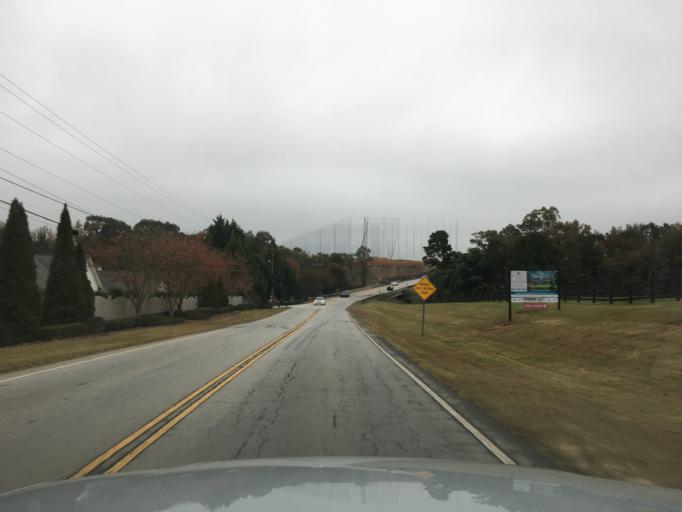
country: US
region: South Carolina
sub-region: Greenville County
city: Five Forks
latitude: 34.8516
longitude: -82.2631
